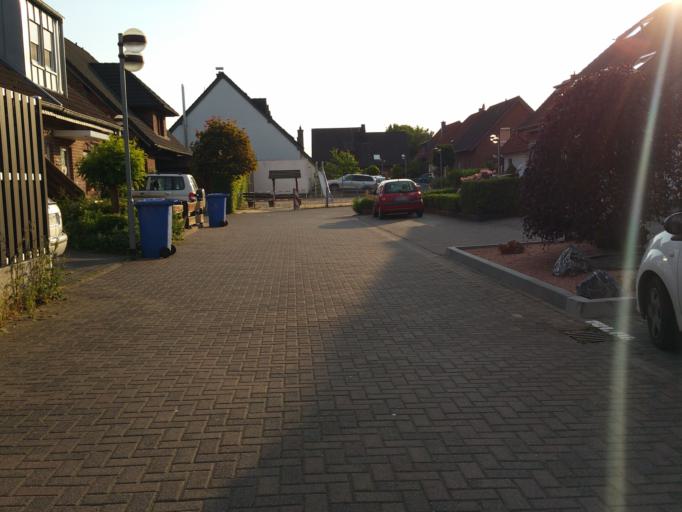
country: DE
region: North Rhine-Westphalia
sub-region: Regierungsbezirk Dusseldorf
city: Grefrath
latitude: 51.3256
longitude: 6.3769
